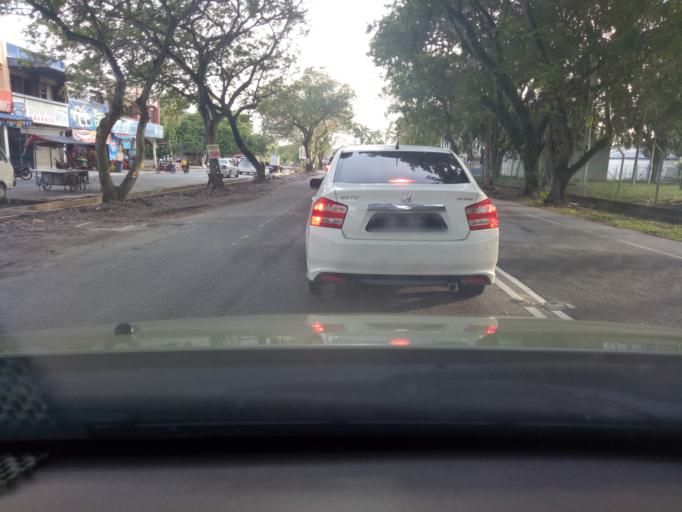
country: MY
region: Kedah
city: Alor Setar
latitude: 6.1279
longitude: 100.3491
